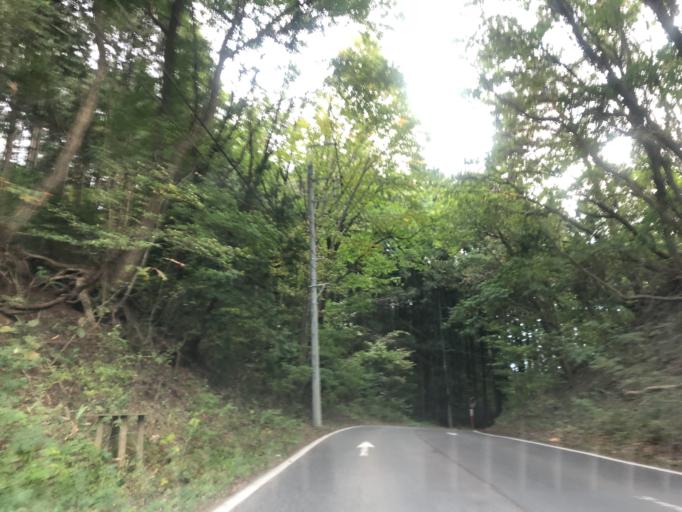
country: JP
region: Tochigi
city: Kuroiso
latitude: 36.9399
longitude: 140.1264
